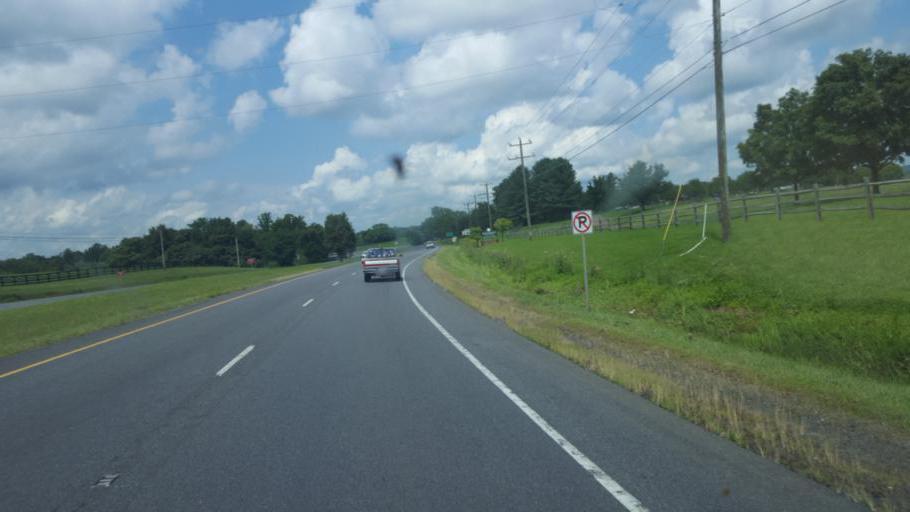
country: US
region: Virginia
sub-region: Fauquier County
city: Marshall
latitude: 38.8257
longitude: -77.8166
